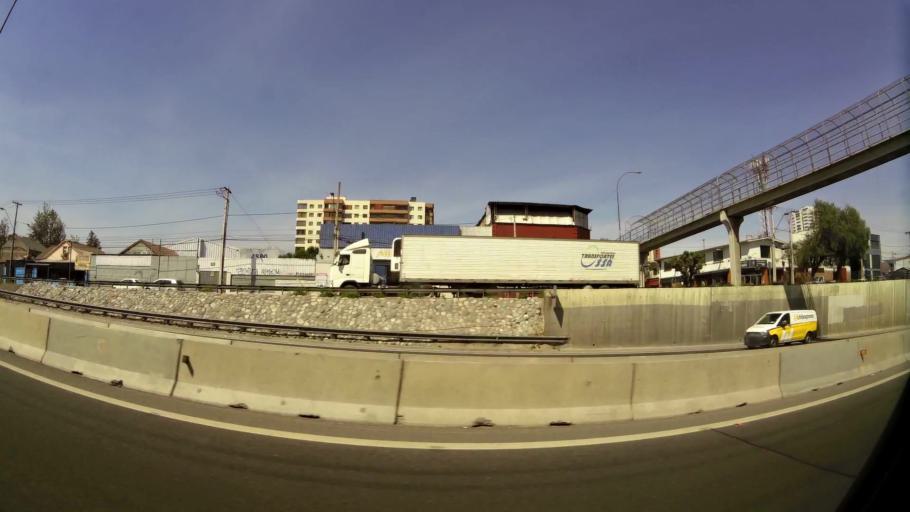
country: CL
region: Santiago Metropolitan
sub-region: Provincia de Santiago
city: Santiago
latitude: -33.4940
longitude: -70.6633
